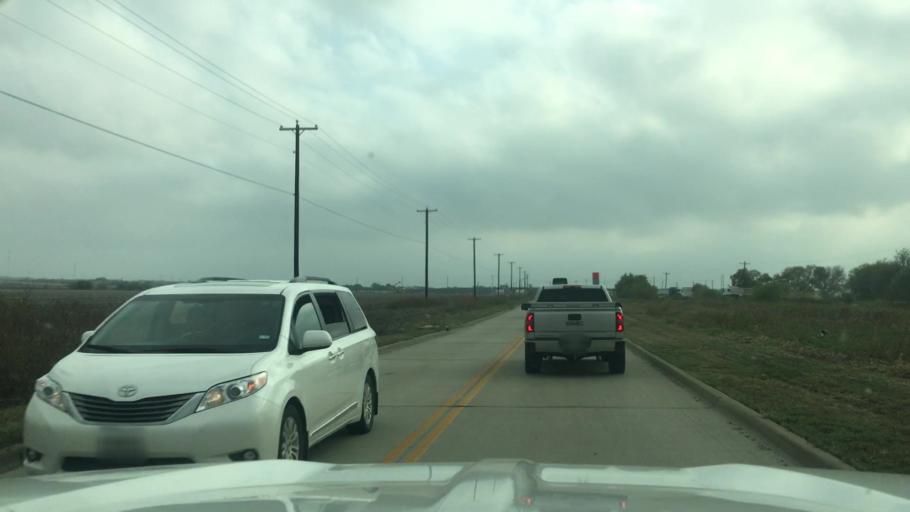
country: US
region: Texas
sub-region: Collin County
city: Prosper
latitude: 33.2275
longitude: -96.8191
